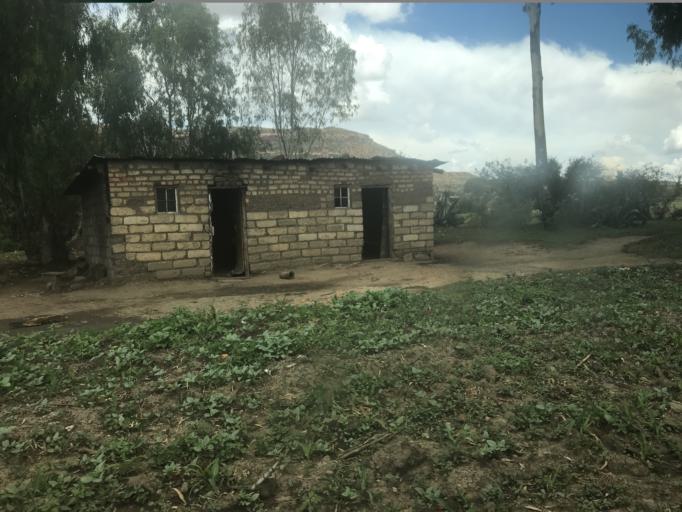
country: LS
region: Maseru
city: Nako
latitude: -29.6190
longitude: 27.5060
